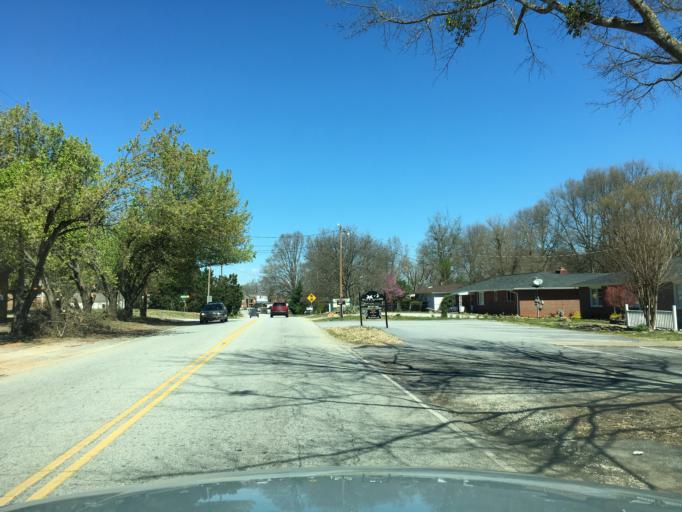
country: US
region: South Carolina
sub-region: Spartanburg County
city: Fairforest
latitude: 34.9288
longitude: -82.0011
